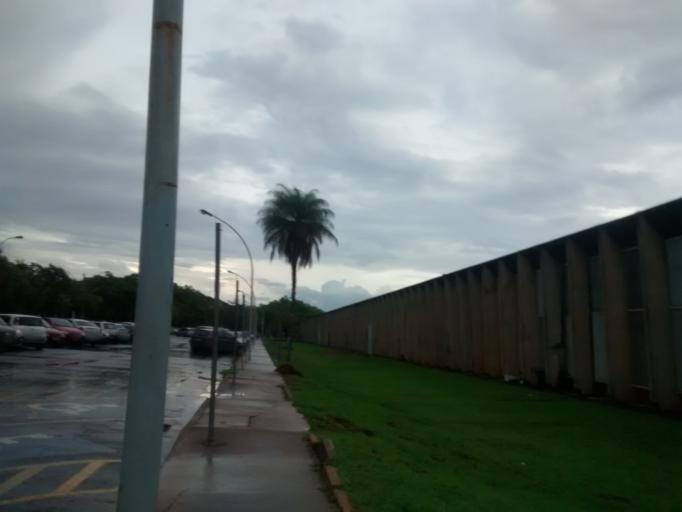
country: BR
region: Federal District
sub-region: Brasilia
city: Brasilia
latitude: -15.7659
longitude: -47.8672
